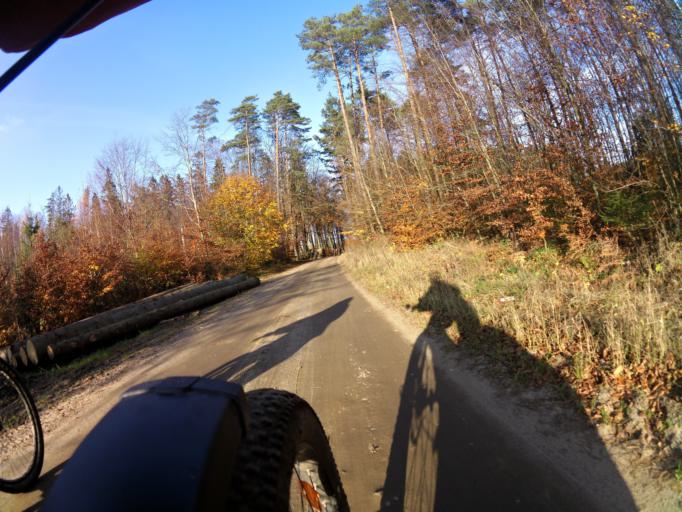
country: PL
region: Pomeranian Voivodeship
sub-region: Powiat pucki
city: Krokowa
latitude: 54.7274
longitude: 18.2158
